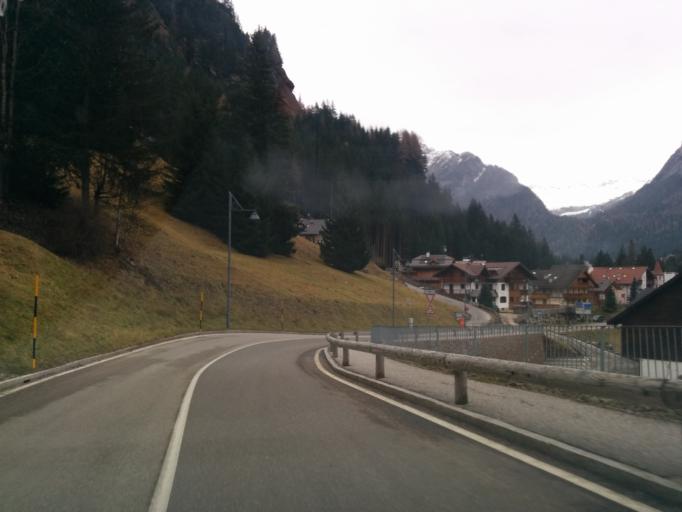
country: IT
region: Trentino-Alto Adige
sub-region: Provincia di Trento
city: Canazei
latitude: 46.4744
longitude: 11.7764
